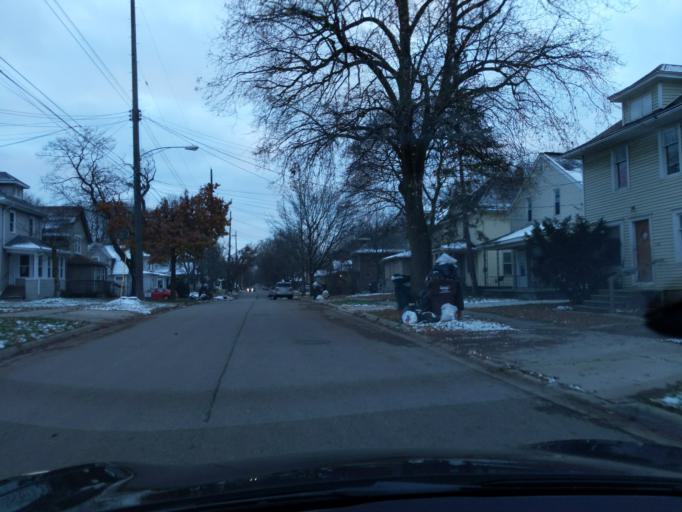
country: US
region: Michigan
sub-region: Ingham County
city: Lansing
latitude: 42.7472
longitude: -84.5348
